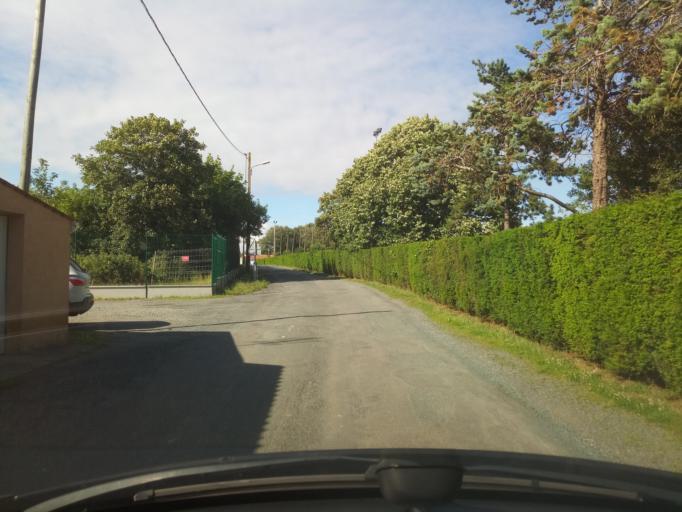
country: FR
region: Poitou-Charentes
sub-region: Departement de la Charente-Maritime
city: Marans
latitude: 46.3021
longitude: -0.9946
